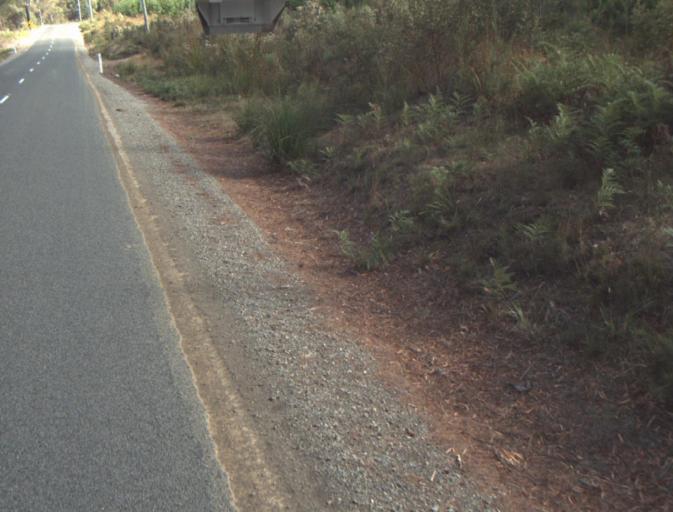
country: AU
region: Tasmania
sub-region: Dorset
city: Bridport
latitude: -41.1435
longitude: 147.2292
